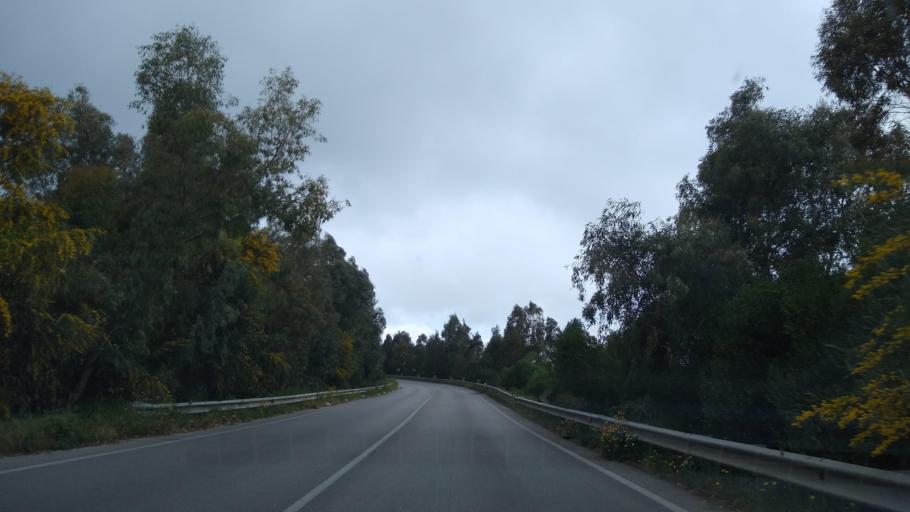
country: IT
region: Sicily
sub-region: Trapani
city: Alcamo
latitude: 37.9917
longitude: 12.9561
